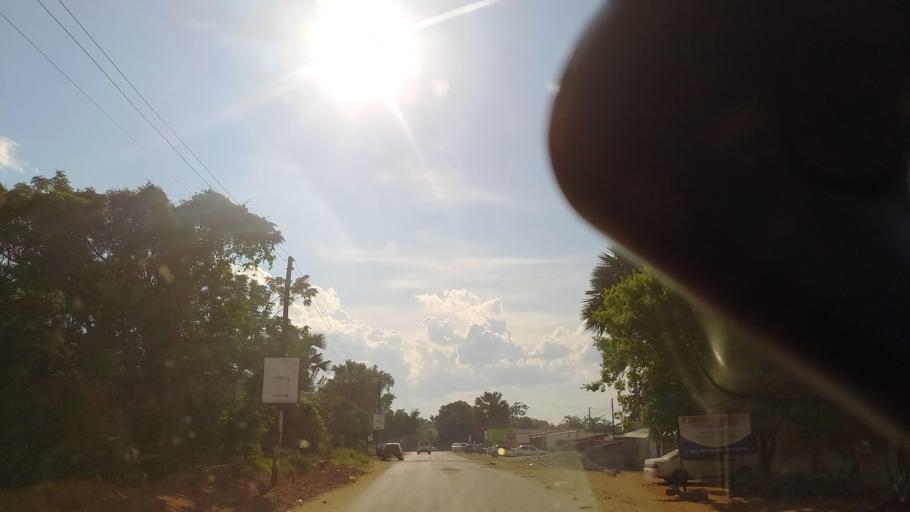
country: ZM
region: Southern
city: Mazabuka
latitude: -15.8612
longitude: 27.7621
